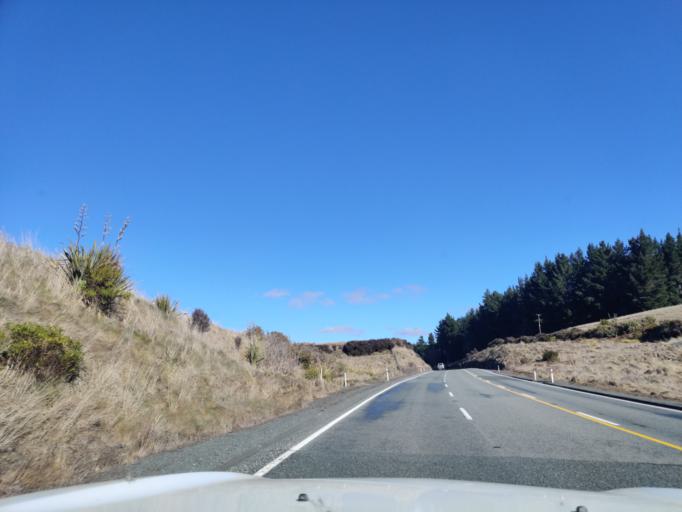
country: NZ
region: Manawatu-Wanganui
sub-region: Ruapehu District
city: Waiouru
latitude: -39.4471
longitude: 175.6799
